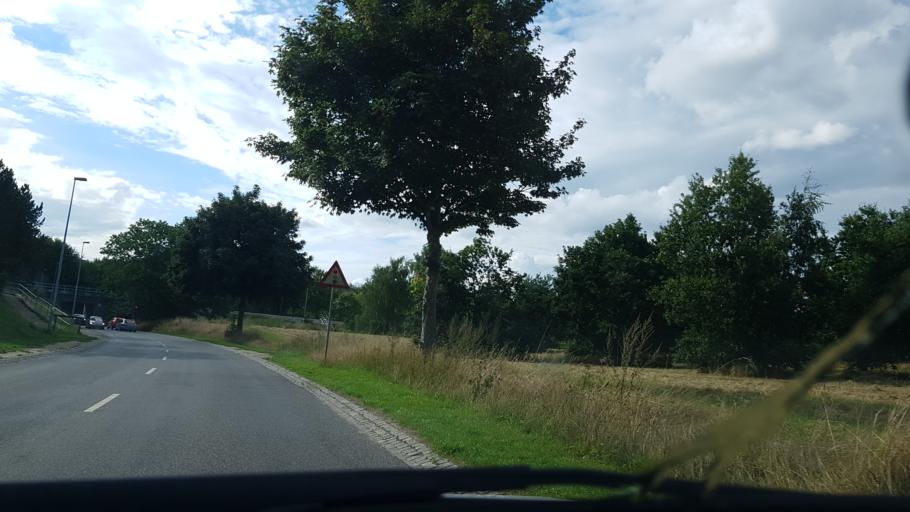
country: DK
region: Capital Region
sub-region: Fredensborg Kommune
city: Kokkedal
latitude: 55.9155
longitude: 12.5029
